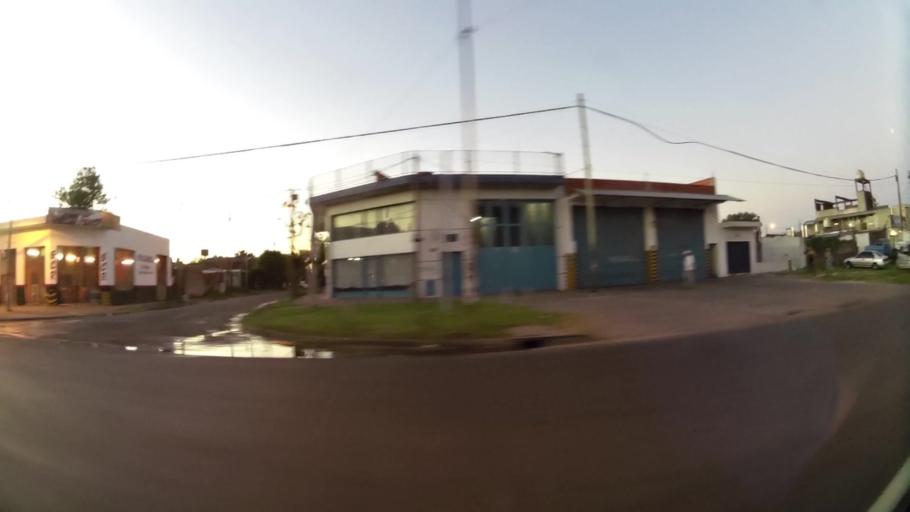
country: AR
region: Buenos Aires
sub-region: Partido de Moron
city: Moron
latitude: -34.7007
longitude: -58.6104
